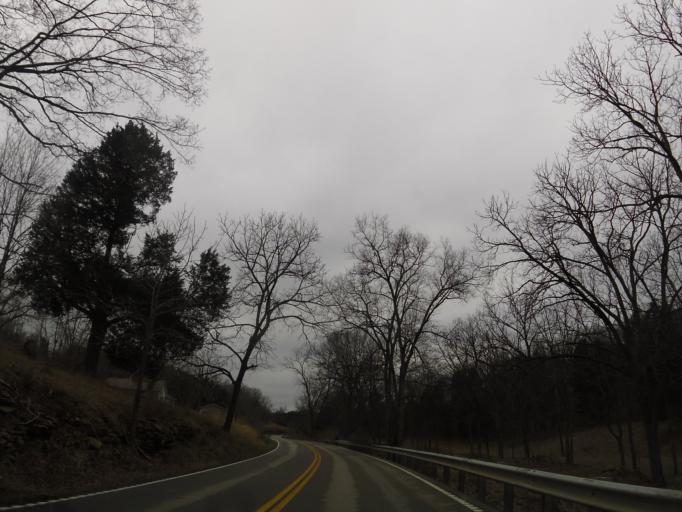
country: US
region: Kentucky
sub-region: Franklin County
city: Frankfort
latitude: 38.2588
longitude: -84.9371
